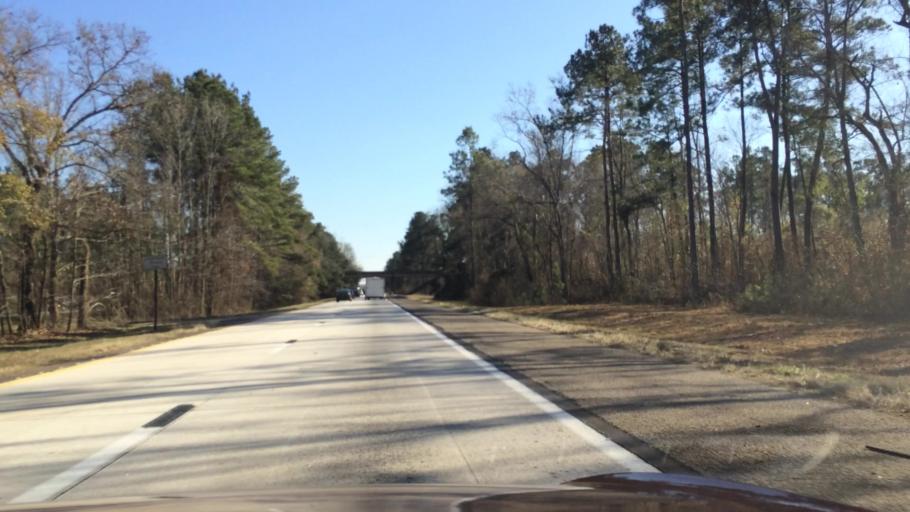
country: US
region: South Carolina
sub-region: Orangeburg County
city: Holly Hill
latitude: 33.2570
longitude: -80.4743
